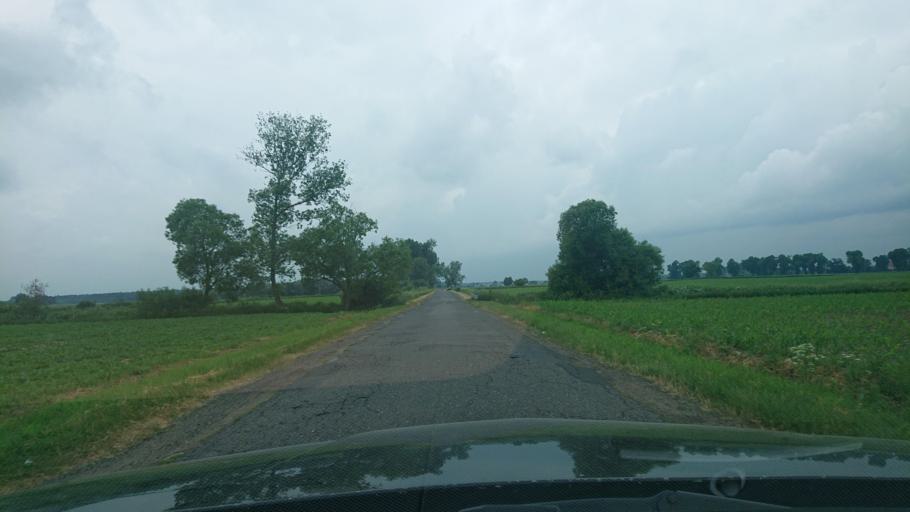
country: PL
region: Greater Poland Voivodeship
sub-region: Powiat gnieznienski
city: Czerniejewo
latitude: 52.4615
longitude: 17.5283
